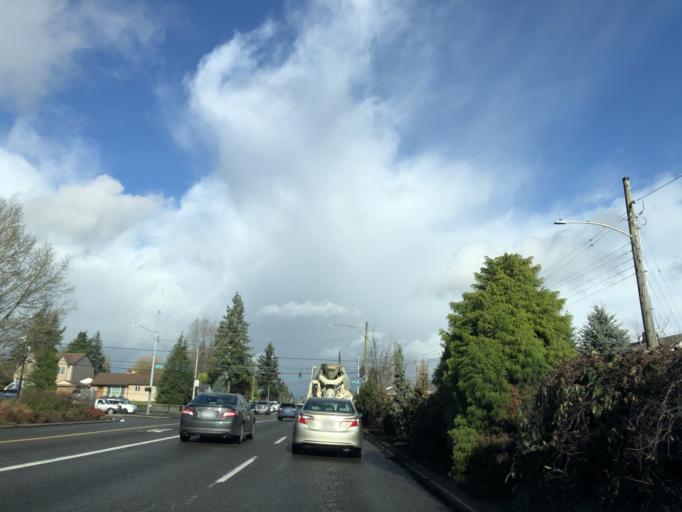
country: US
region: Washington
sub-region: Pierce County
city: Tacoma
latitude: 47.2420
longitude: -122.4629
